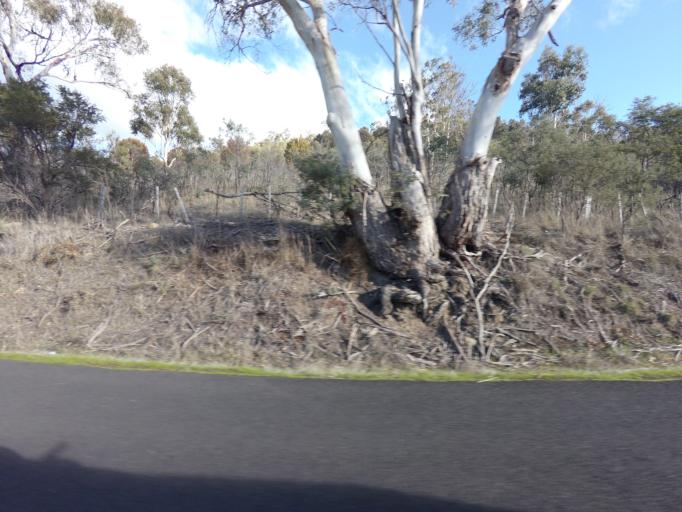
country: AU
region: Tasmania
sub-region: Derwent Valley
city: New Norfolk
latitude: -42.7454
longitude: 147.0411
